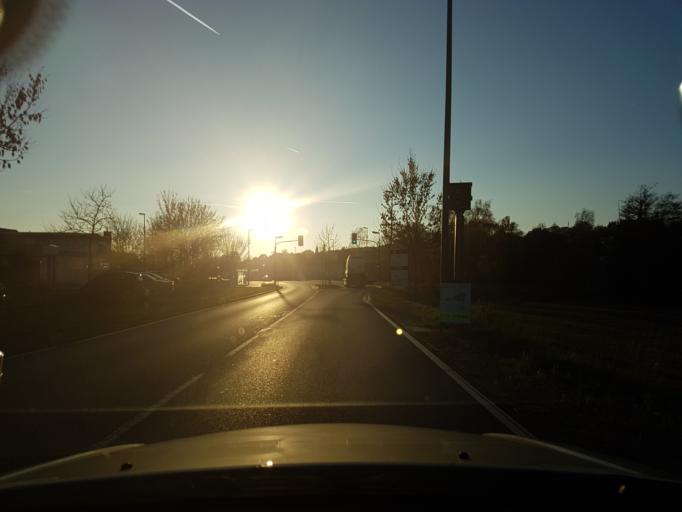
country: DE
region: Hesse
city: Taunusstein
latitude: 50.1718
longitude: 8.2132
